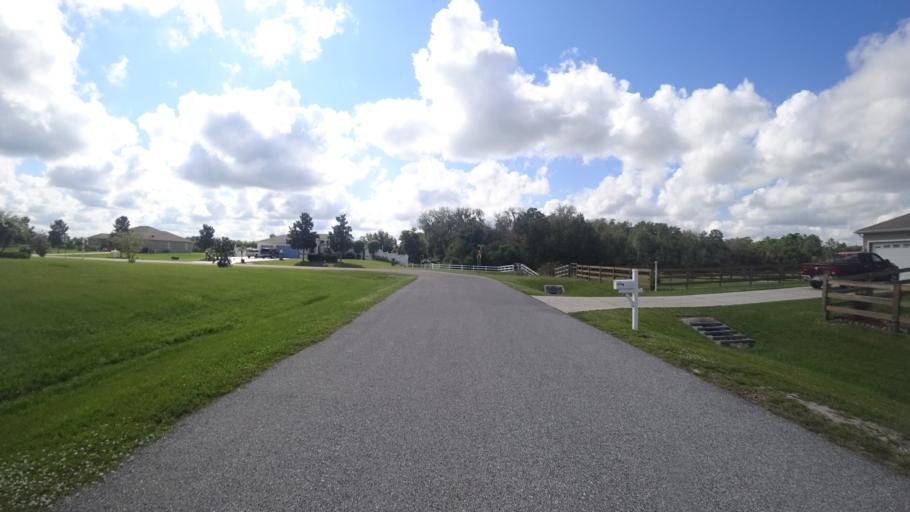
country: US
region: Florida
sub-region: Sarasota County
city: Lake Sarasota
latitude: 27.3925
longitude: -82.2763
